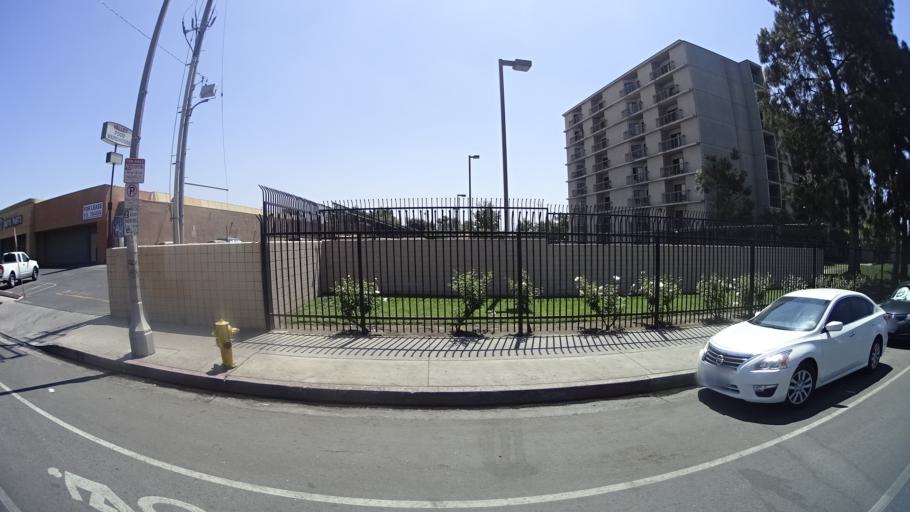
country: US
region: California
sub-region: Los Angeles County
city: Van Nuys
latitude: 34.2341
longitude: -118.4502
